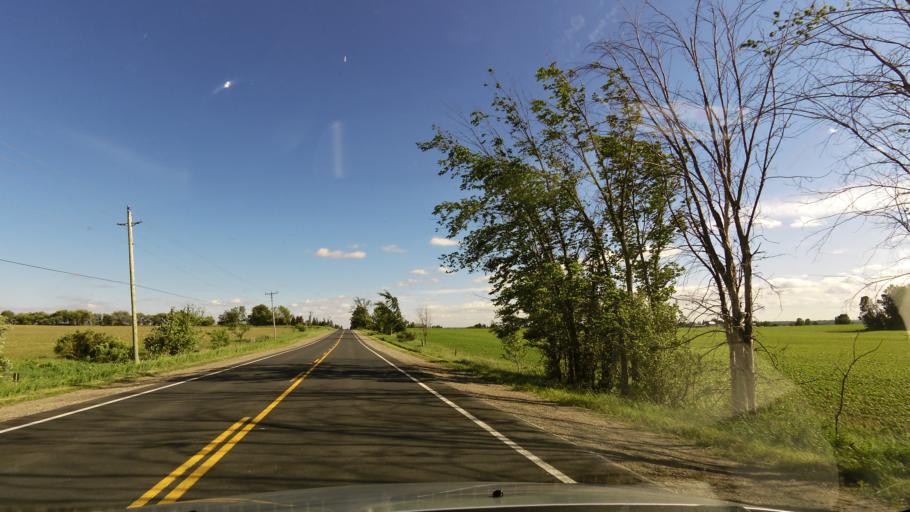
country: CA
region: Ontario
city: Bradford West Gwillimbury
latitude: 44.0739
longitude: -79.6721
